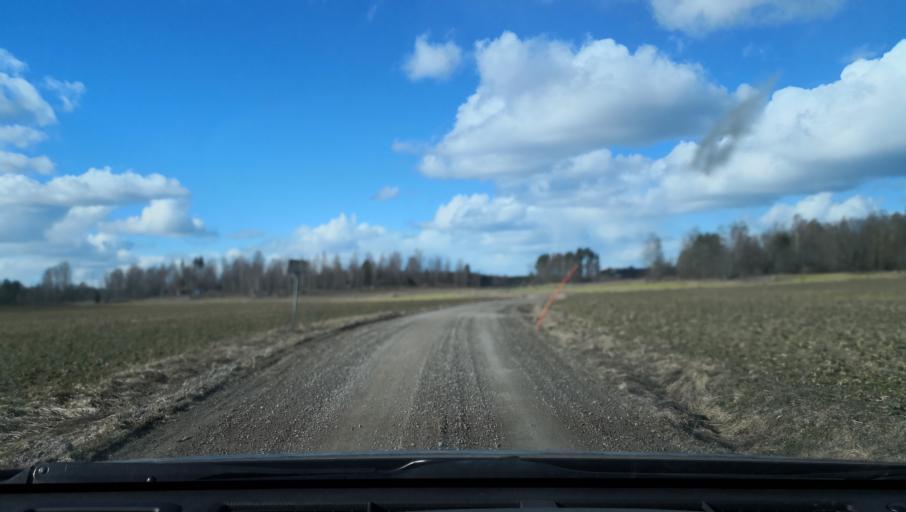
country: SE
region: OErebro
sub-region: Lindesbergs Kommun
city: Fellingsbro
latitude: 59.4213
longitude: 15.6297
